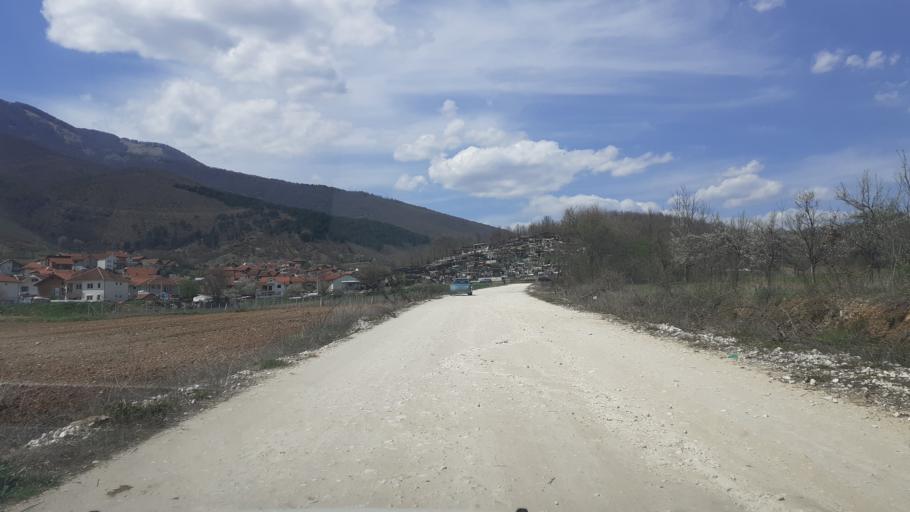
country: MK
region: Makedonski Brod
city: Makedonski Brod
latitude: 41.5156
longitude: 21.2212
